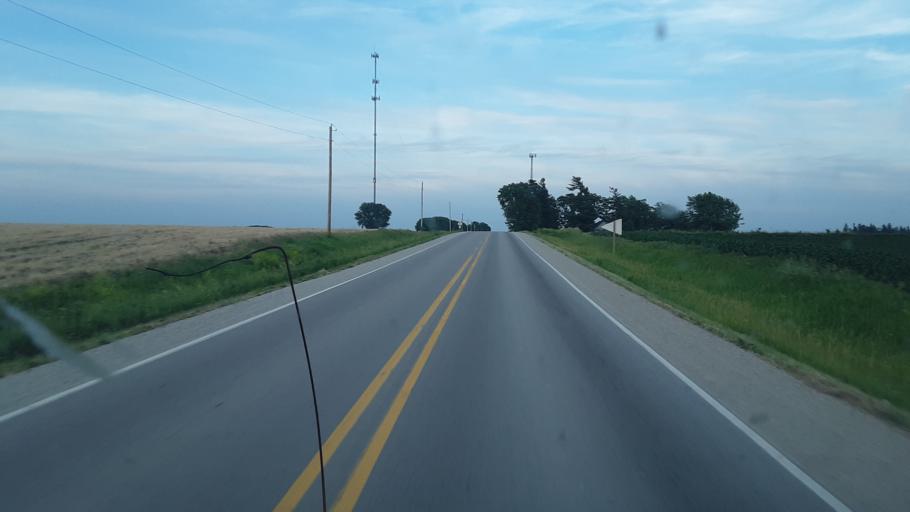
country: US
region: Iowa
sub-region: Iowa County
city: Marengo
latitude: 41.7028
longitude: -92.1785
